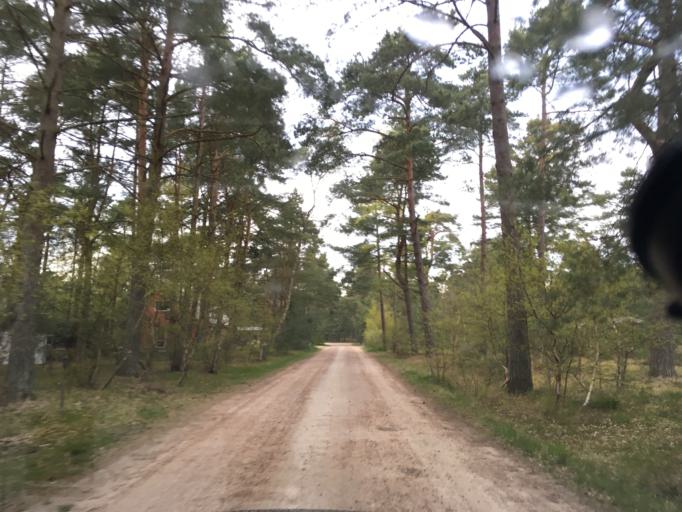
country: SE
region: Skane
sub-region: Vellinge Kommun
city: Ljunghusen
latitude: 55.4001
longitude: 12.9291
